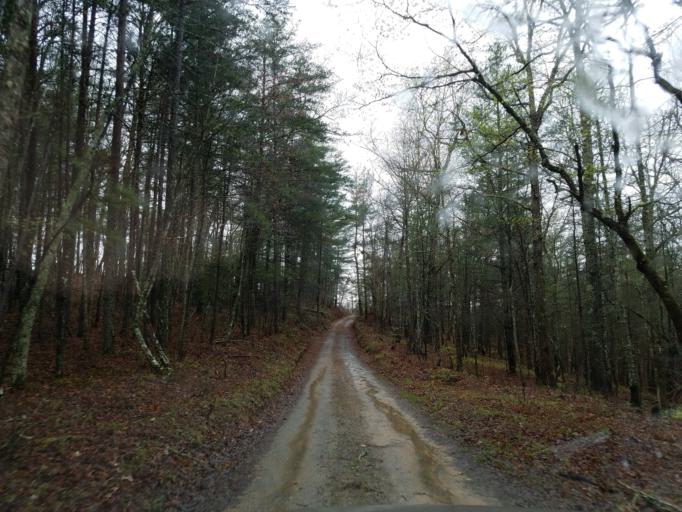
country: US
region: Georgia
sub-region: Fannin County
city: Blue Ridge
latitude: 34.8316
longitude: -84.2376
